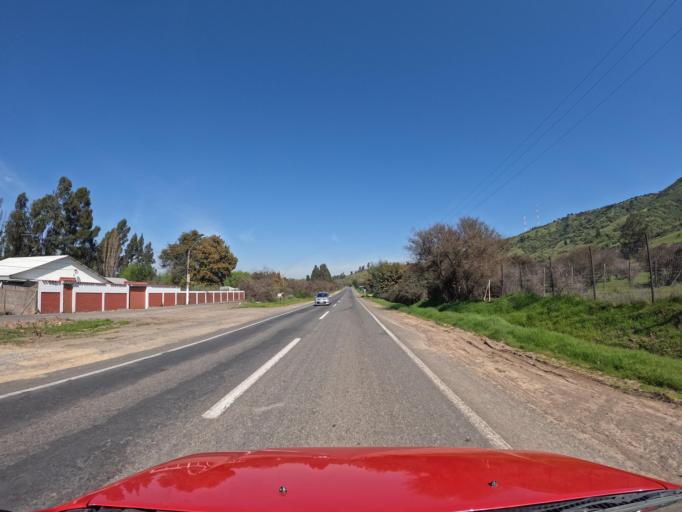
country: CL
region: Maule
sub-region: Provincia de Talca
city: Talca
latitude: -35.0819
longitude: -71.6388
